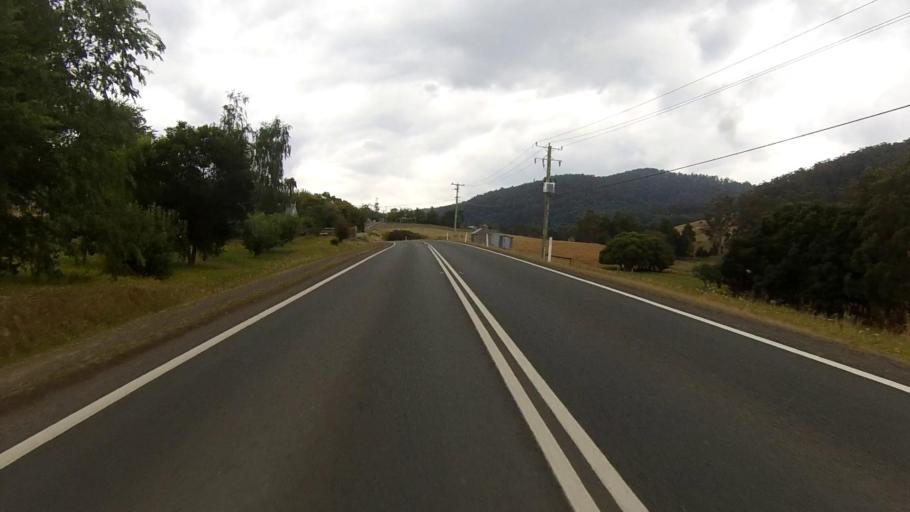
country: AU
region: Tasmania
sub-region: Huon Valley
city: Cygnet
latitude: -43.1493
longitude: 147.0689
